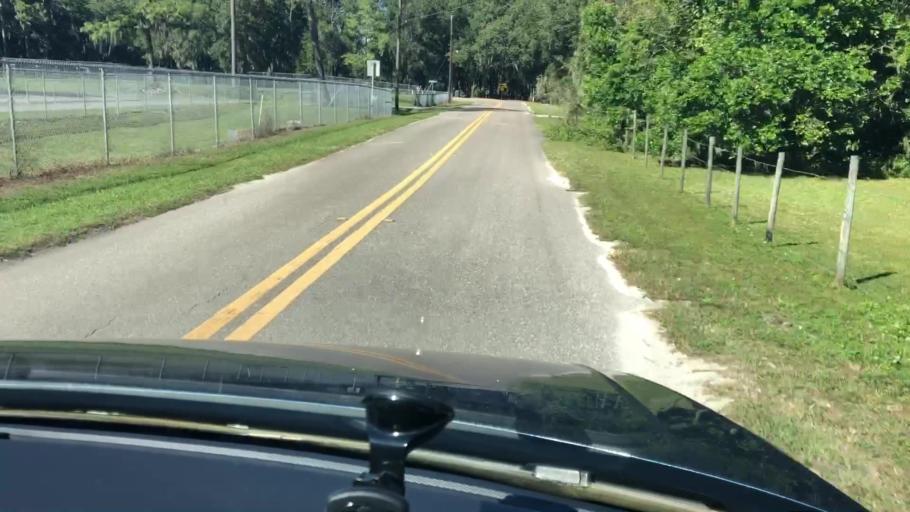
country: US
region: Florida
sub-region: Polk County
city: Kathleen
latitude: 28.1269
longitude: -82.0171
